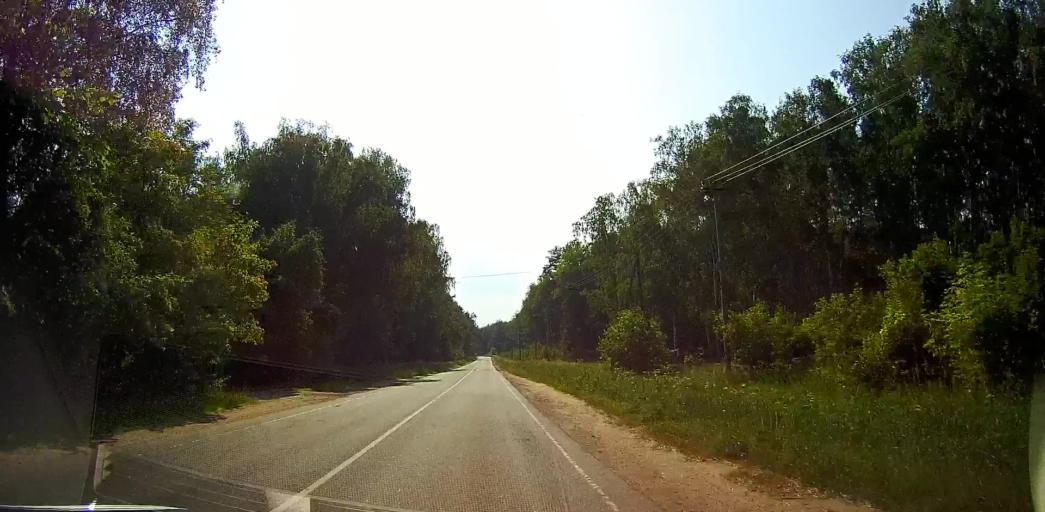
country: RU
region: Moskovskaya
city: Il'inskoye
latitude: 55.2849
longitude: 37.9336
